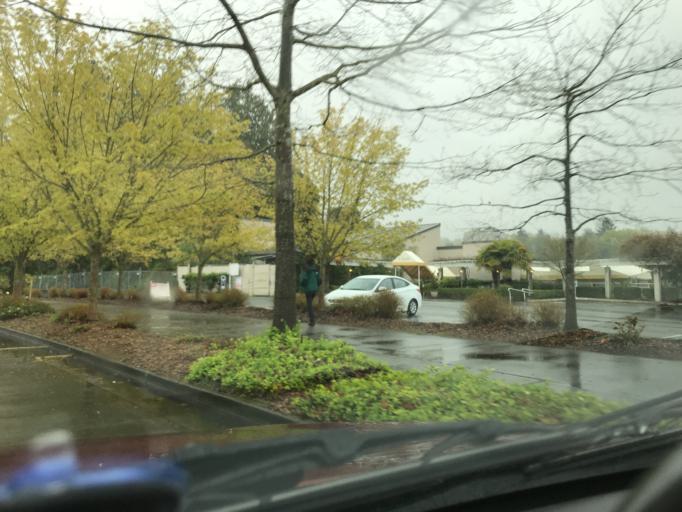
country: US
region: Washington
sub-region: King County
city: Seattle
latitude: 47.6676
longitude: -122.4008
